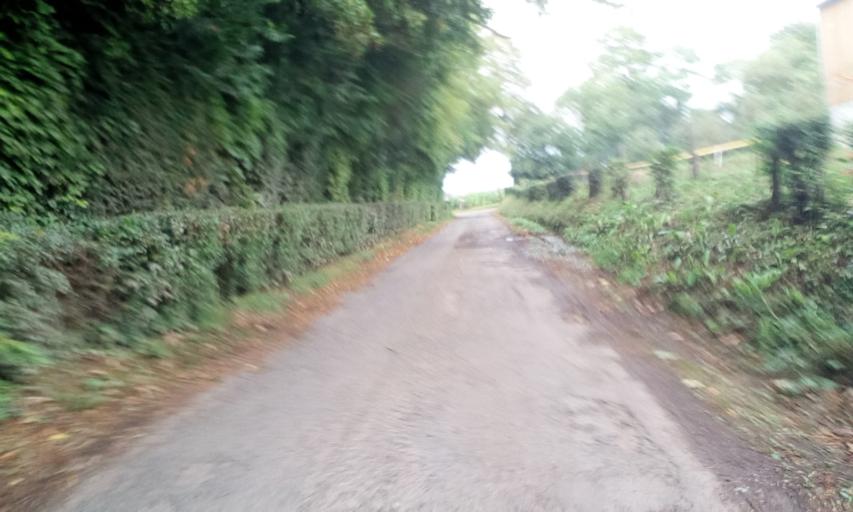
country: FR
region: Lower Normandy
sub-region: Departement du Calvados
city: Tilly-sur-Seulles
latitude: 49.2182
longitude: -0.6235
